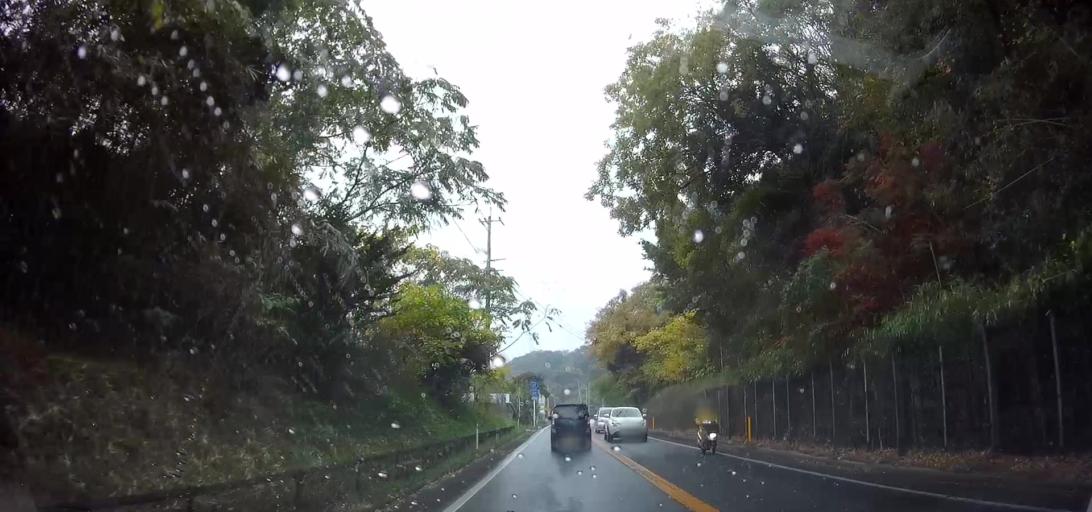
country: JP
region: Nagasaki
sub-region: Isahaya-shi
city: Isahaya
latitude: 32.7957
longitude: 130.1787
